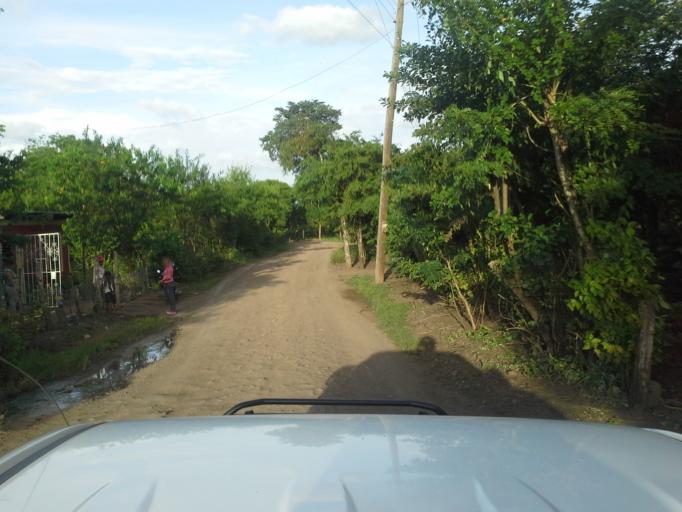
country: NI
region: Matagalpa
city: Ciudad Dario
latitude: 12.7921
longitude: -86.1533
